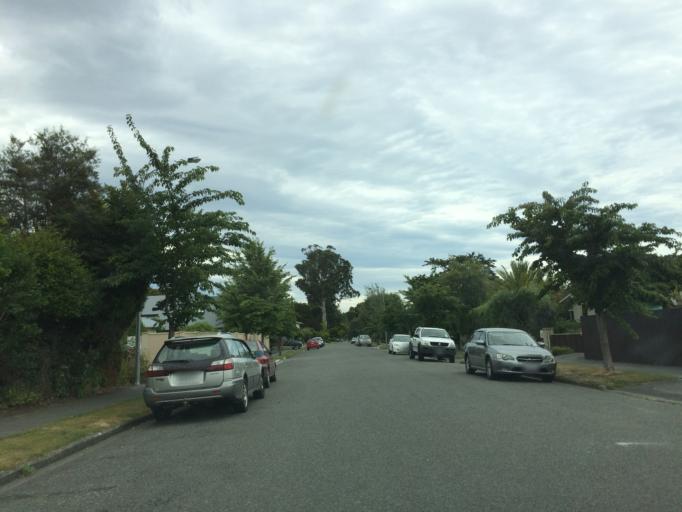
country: NZ
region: Canterbury
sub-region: Selwyn District
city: Prebbleton
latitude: -43.5214
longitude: 172.5465
